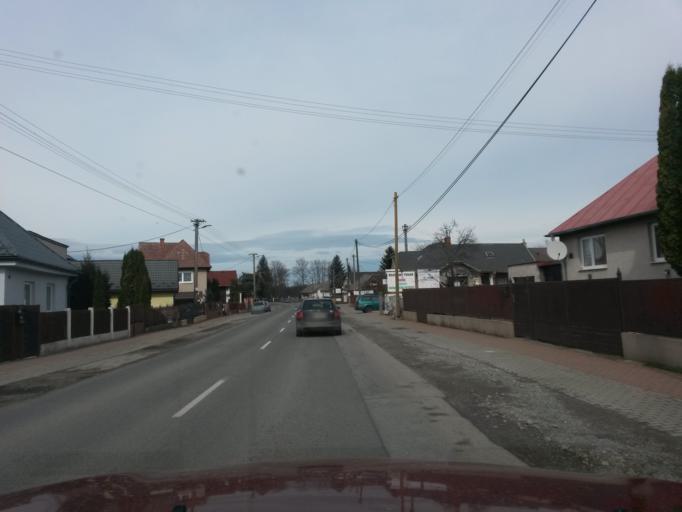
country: SK
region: Kosicky
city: Kosice
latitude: 48.6444
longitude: 21.2903
